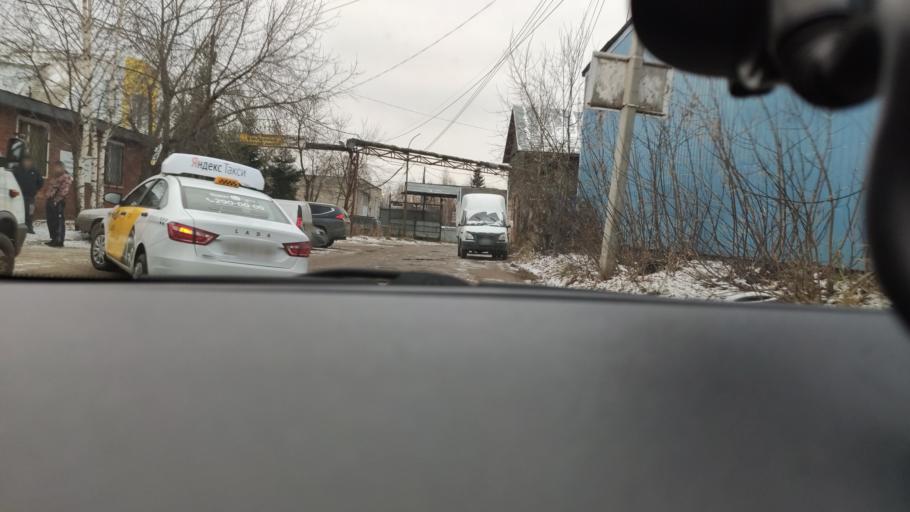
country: RU
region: Perm
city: Perm
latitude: 57.9846
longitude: 56.2758
